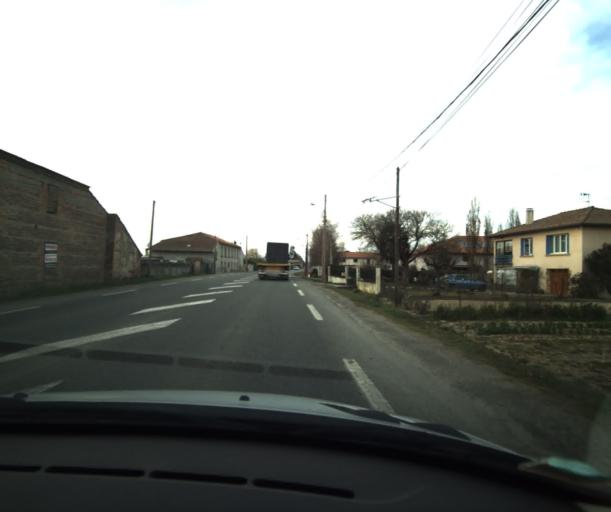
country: FR
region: Midi-Pyrenees
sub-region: Departement du Tarn-et-Garonne
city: Saint-Porquier
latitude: 44.0094
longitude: 1.1742
